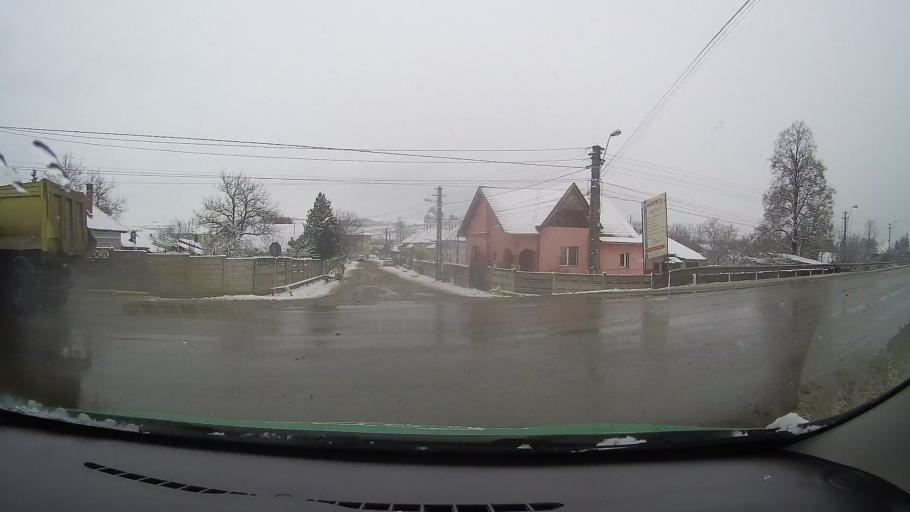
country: RO
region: Hunedoara
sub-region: Municipiul Hunedoara
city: Pestisu Mare
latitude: 45.8034
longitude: 22.9234
